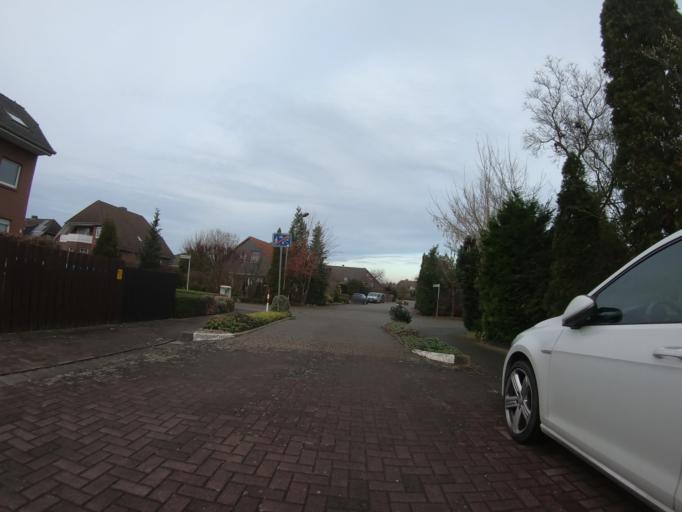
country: DE
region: Lower Saxony
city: Isenbuttel
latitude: 52.4296
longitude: 10.5879
